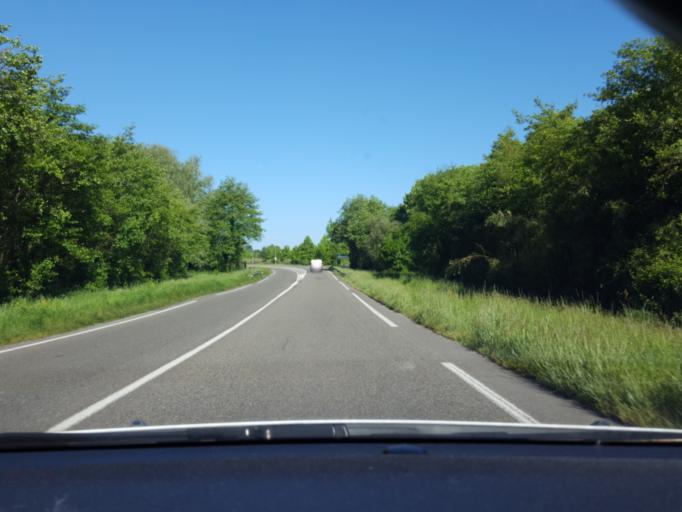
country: FR
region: Aquitaine
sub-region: Departement des Landes
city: Tarnos
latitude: 43.5496
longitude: -1.4521
